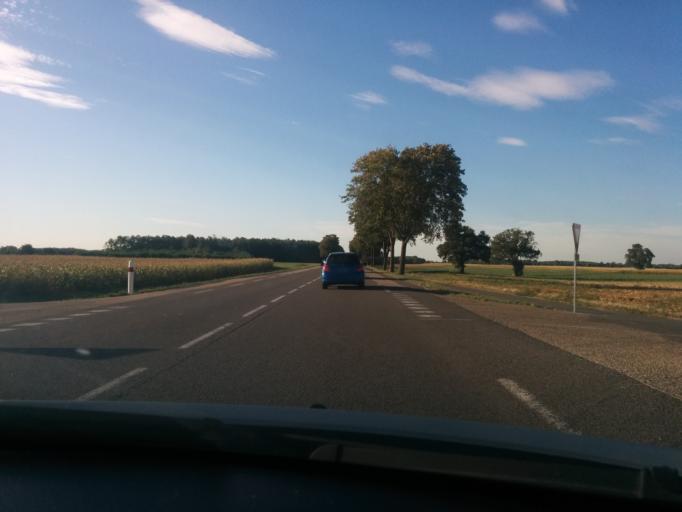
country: FR
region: Rhone-Alpes
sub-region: Departement de l'Ain
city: Tossiat
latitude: 46.1184
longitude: 5.2975
